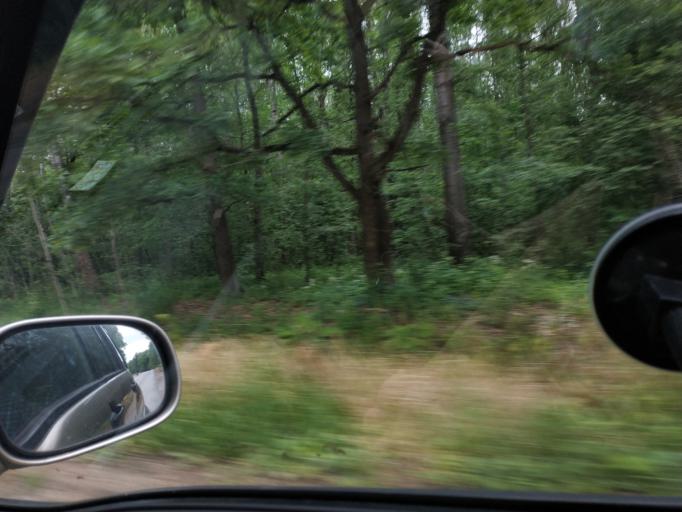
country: RU
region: Moskovskaya
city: Krasnoarmeysk
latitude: 56.0771
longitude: 38.2444
